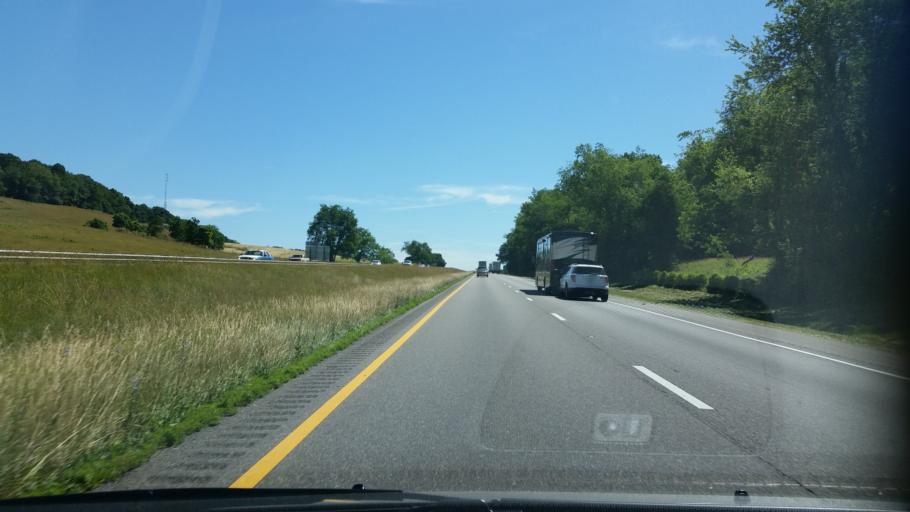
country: US
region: Virginia
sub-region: Washington County
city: Emory
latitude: 36.7615
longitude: -81.8446
